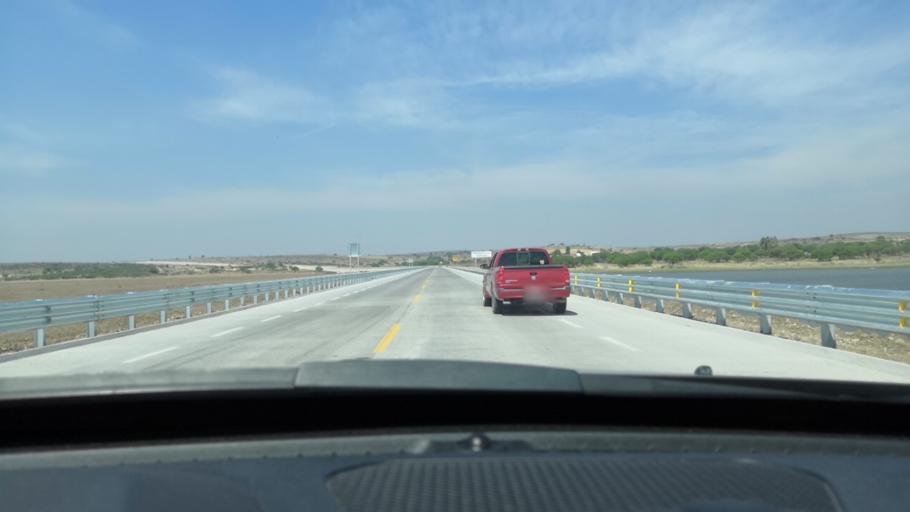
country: MX
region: Guanajuato
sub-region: Purisima del Rincon
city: Potrerillos (Guanajal)
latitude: 21.0849
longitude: -101.8444
